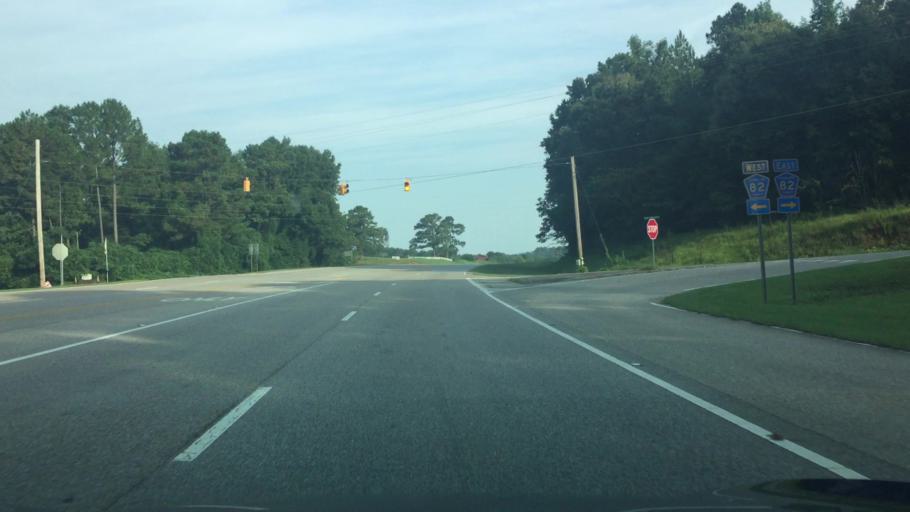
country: US
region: Alabama
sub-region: Covington County
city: Andalusia
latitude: 31.4067
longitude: -86.6015
